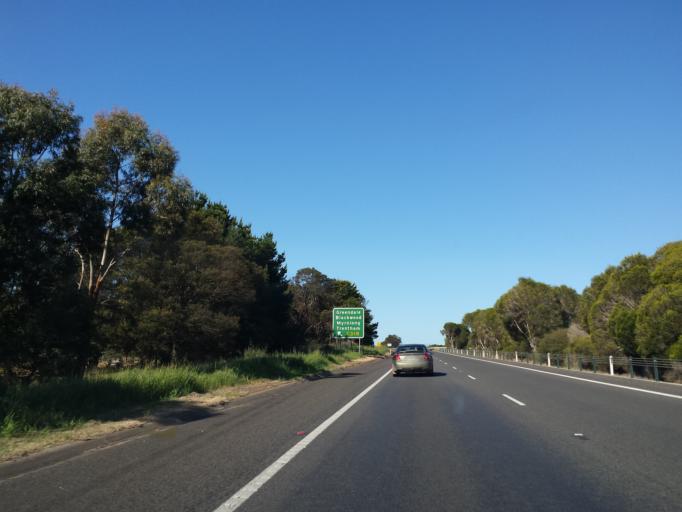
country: AU
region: Victoria
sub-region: Moorabool
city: Bacchus Marsh
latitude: -37.6097
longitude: 144.3122
